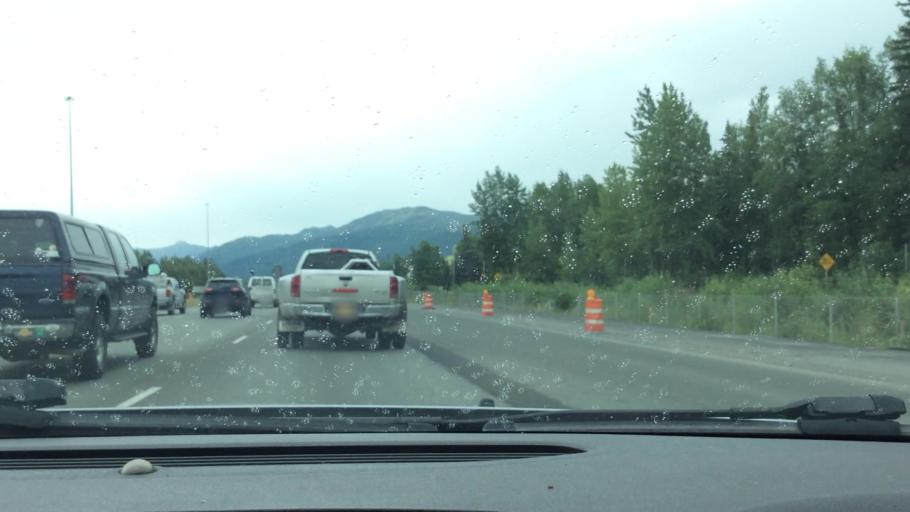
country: US
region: Alaska
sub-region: Anchorage Municipality
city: Elmendorf Air Force Base
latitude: 61.2287
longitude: -149.7257
